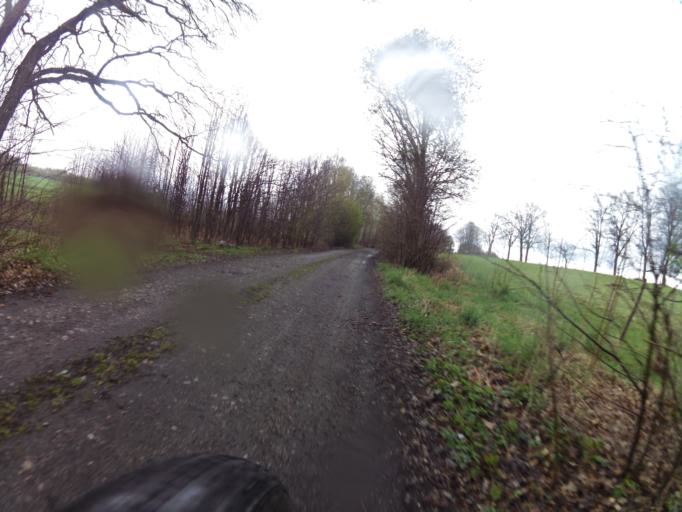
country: PL
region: Pomeranian Voivodeship
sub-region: Powiat slupski
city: Kepice
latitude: 54.2761
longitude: 16.7968
